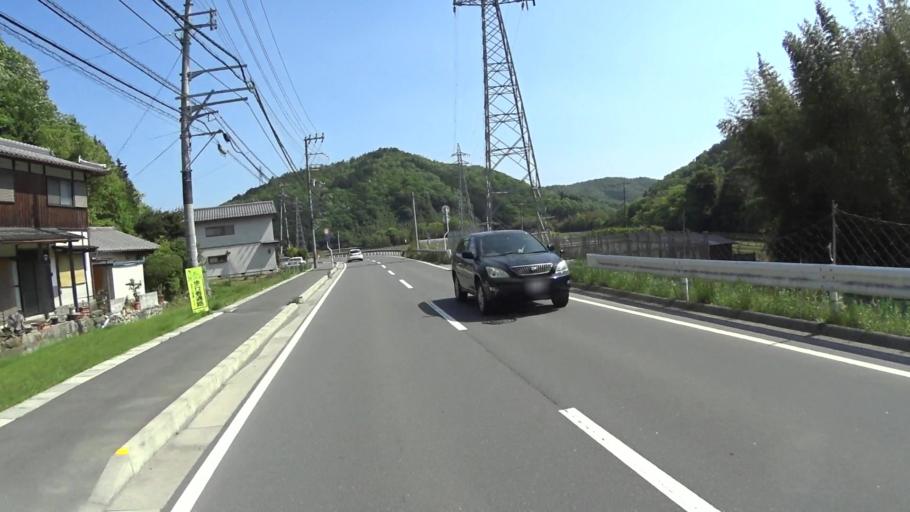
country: JP
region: Kyoto
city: Kameoka
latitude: 35.1215
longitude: 135.5066
